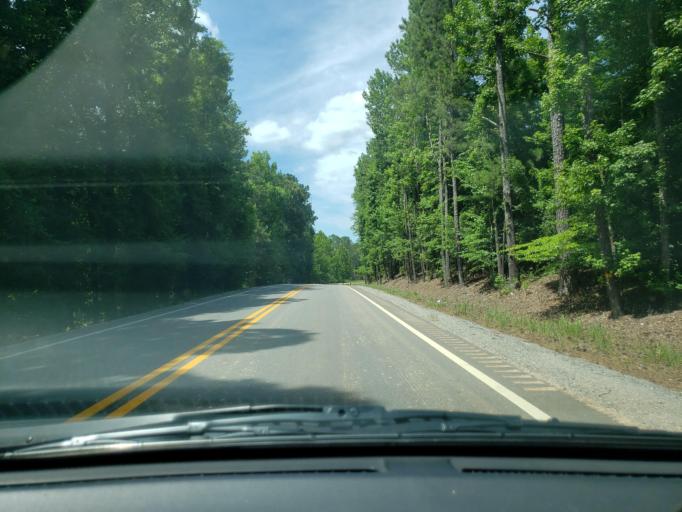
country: US
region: Alabama
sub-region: Elmore County
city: Eclectic
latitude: 32.6389
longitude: -85.9536
